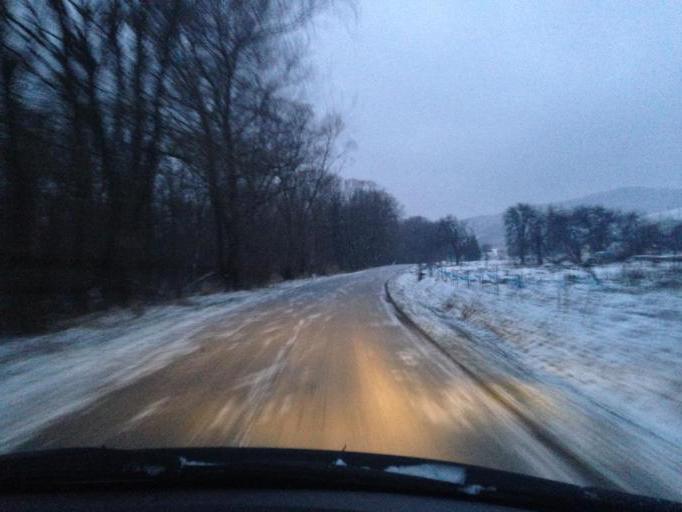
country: PL
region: Subcarpathian Voivodeship
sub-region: Powiat jasielski
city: Krempna
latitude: 49.5313
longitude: 21.5519
